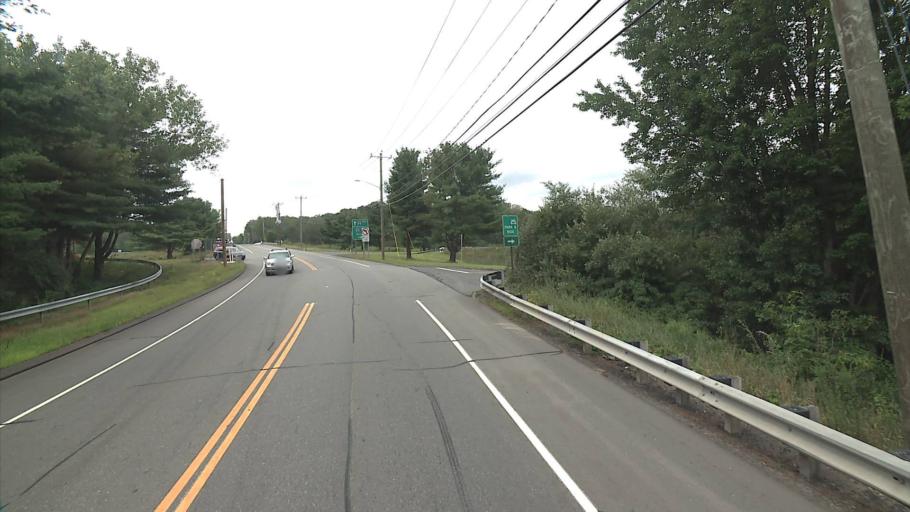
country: US
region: Connecticut
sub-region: Tolland County
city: Tolland
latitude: 41.8853
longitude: -72.3095
